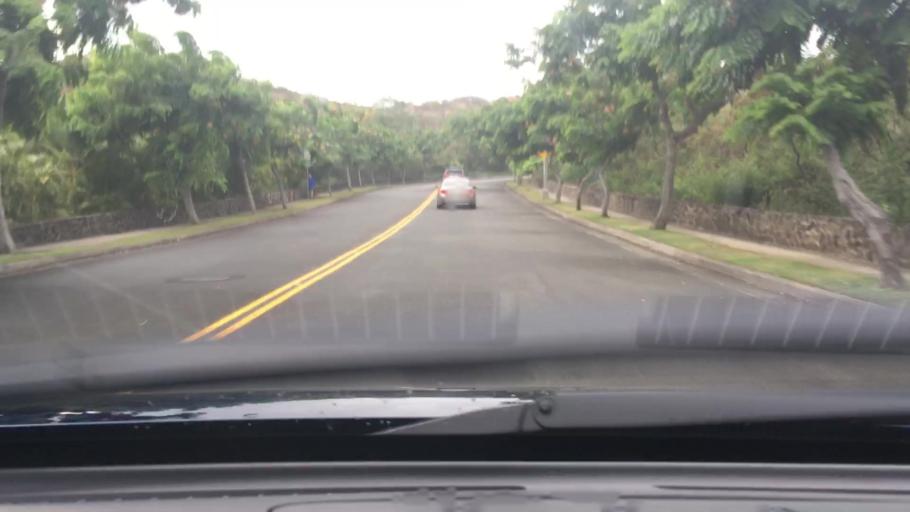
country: US
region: Hawaii
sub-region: Honolulu County
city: Waimanalo Beach
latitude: 21.2890
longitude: -157.7037
